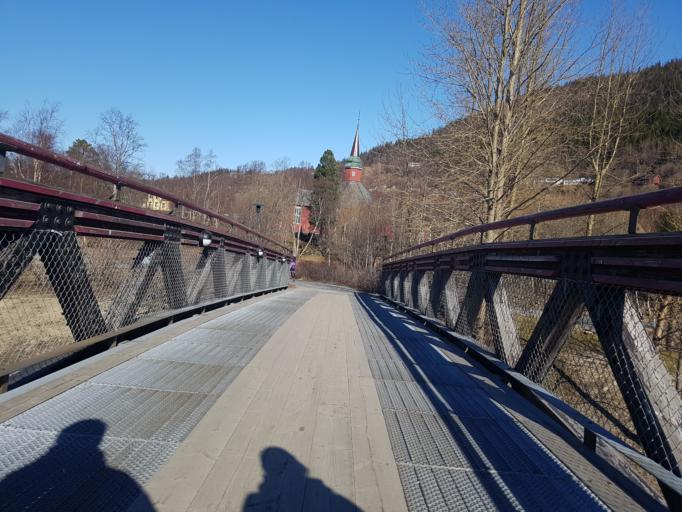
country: NO
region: Nordland
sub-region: Vefsn
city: Mosjoen
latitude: 65.8432
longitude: 13.2036
